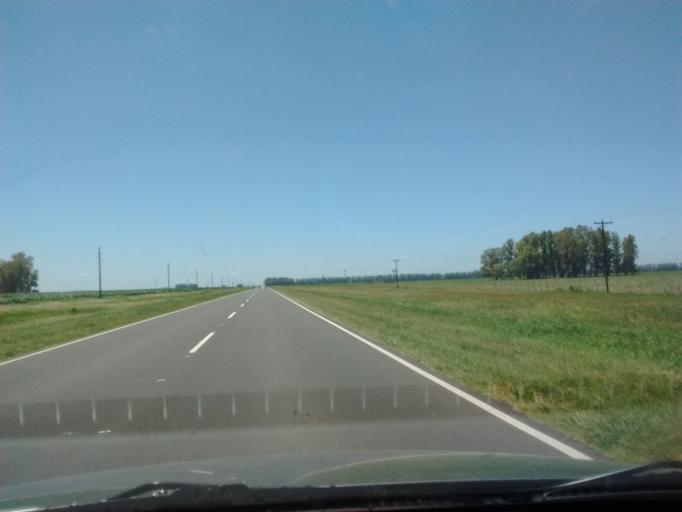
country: AR
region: Entre Rios
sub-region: Departamento de Gualeguay
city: Gualeguay
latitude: -32.9908
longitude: -59.5291
